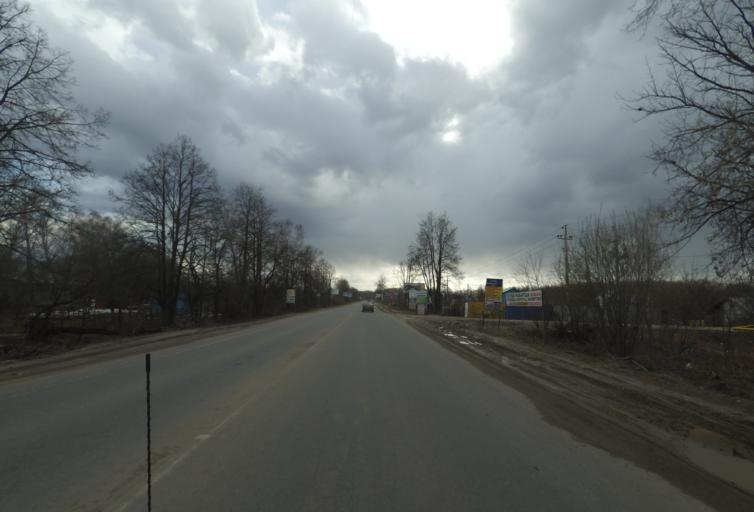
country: RU
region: Nizjnij Novgorod
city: Afonino
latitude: 56.2251
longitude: 44.0923
